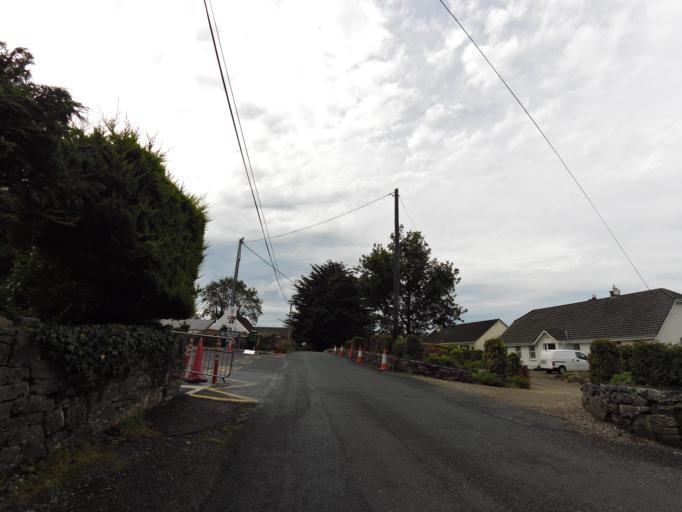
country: IE
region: Connaught
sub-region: County Galway
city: Gaillimh
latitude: 53.3019
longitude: -9.0687
